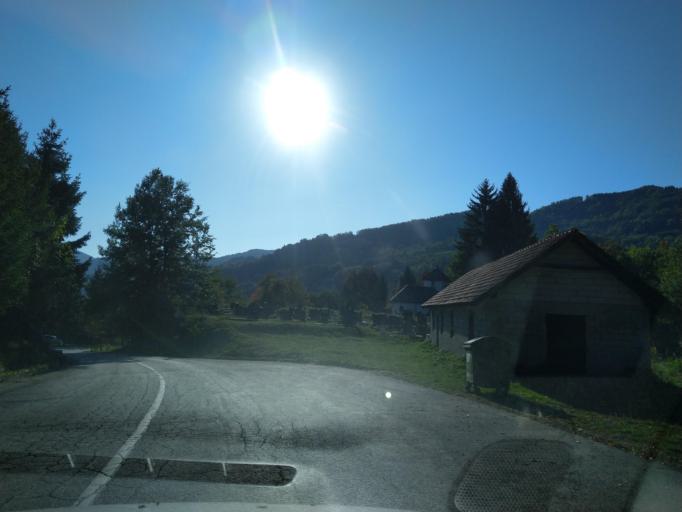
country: RS
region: Central Serbia
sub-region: Moravicki Okrug
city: Ivanjica
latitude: 43.4715
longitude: 20.2397
